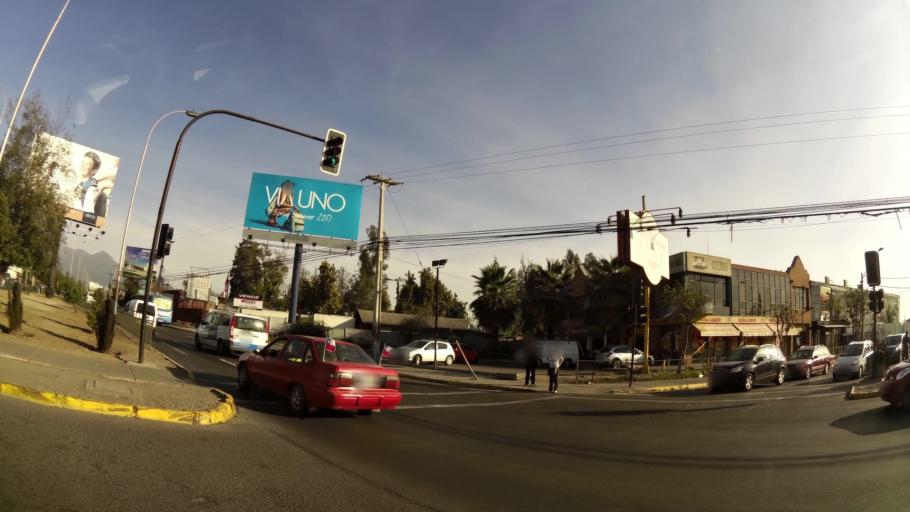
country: CL
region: Santiago Metropolitan
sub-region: Provincia de Cordillera
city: Puente Alto
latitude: -33.5524
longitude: -70.5644
